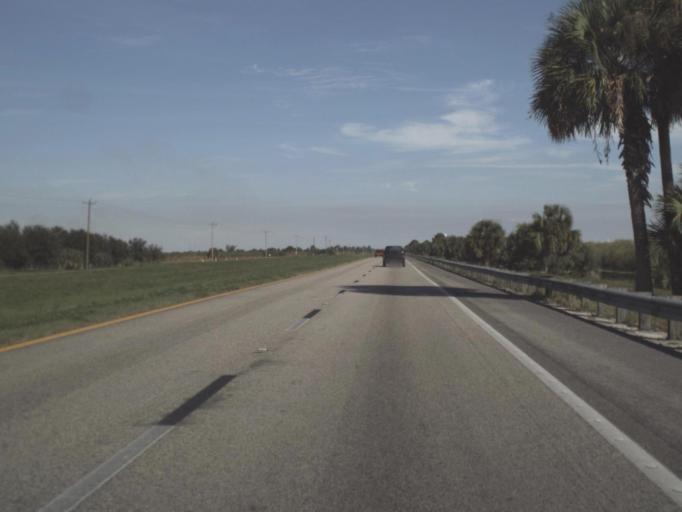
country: US
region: Florida
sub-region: Hendry County
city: Harlem
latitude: 26.7537
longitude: -81.0395
